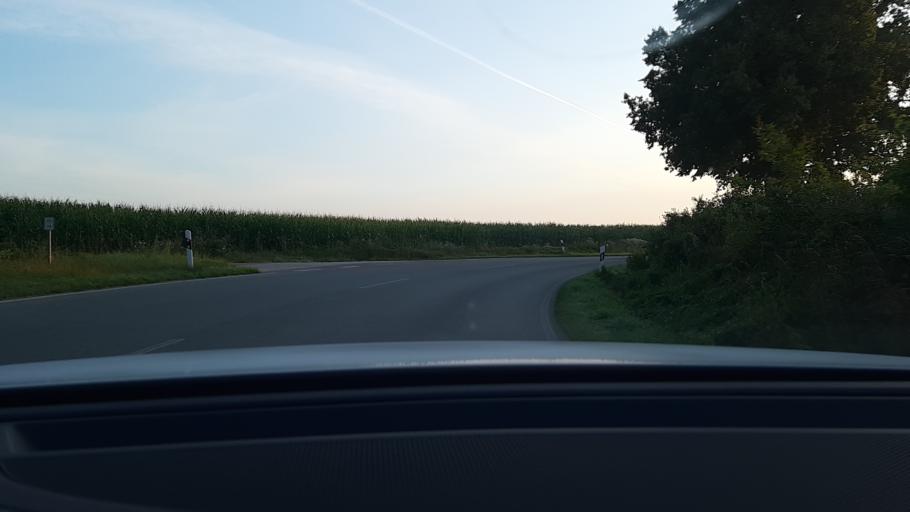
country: DE
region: Schleswig-Holstein
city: Klein Wesenberg
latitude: 53.8242
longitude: 10.5345
